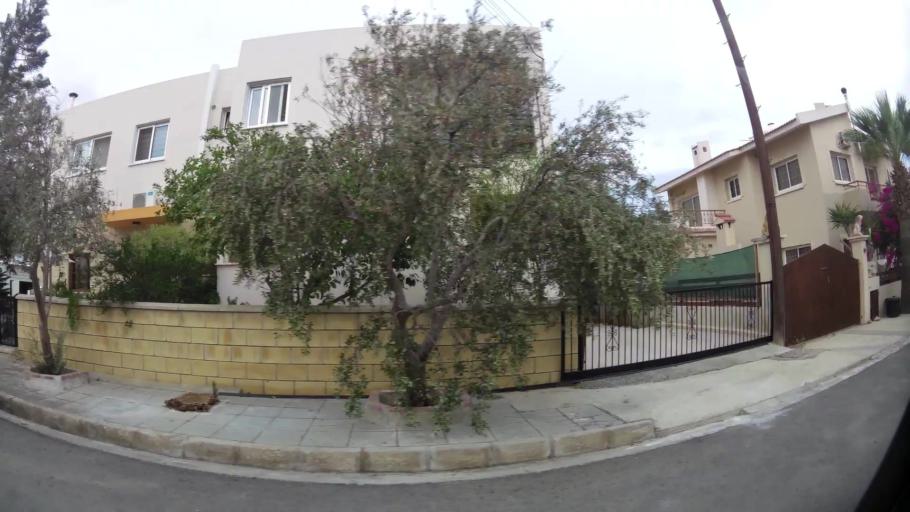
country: CY
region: Lefkosia
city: Geri
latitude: 35.0988
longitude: 33.3941
